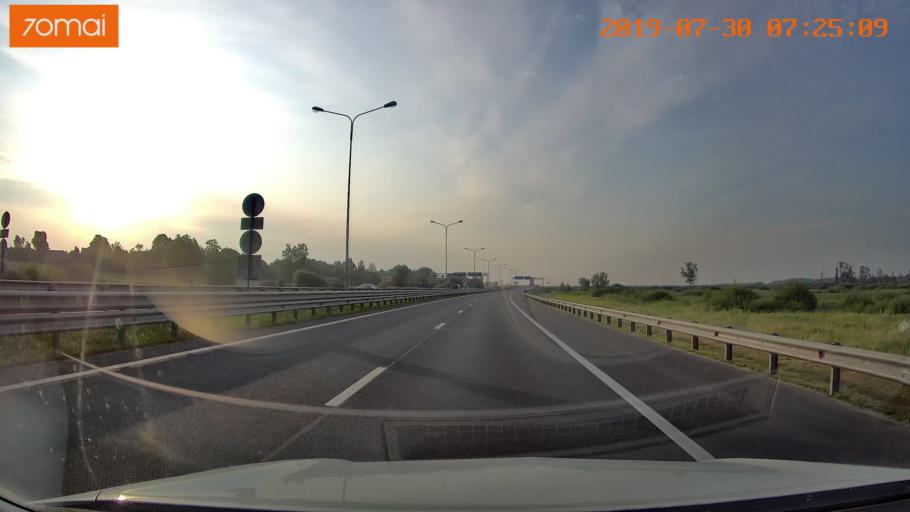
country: RU
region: Kaliningrad
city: Bol'shoe Isakovo
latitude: 54.6885
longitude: 20.8300
